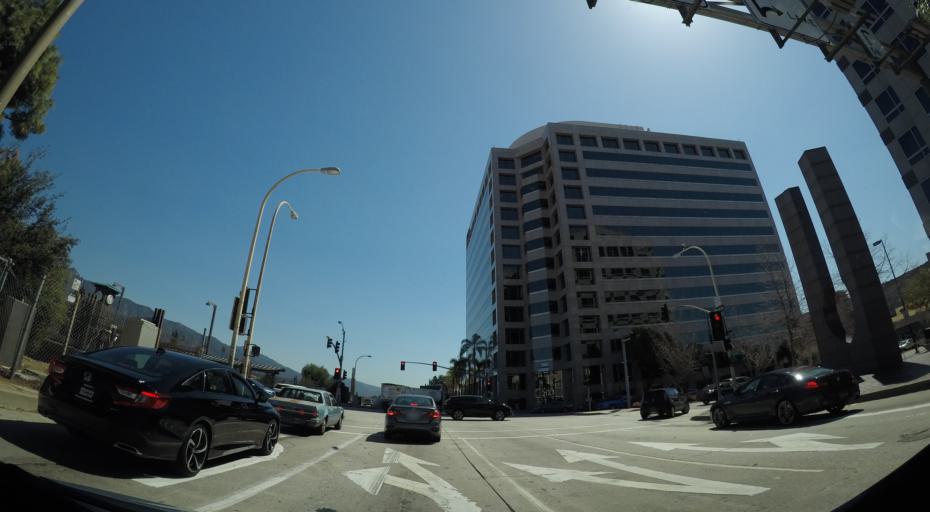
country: US
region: California
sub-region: Los Angeles County
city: Pasadena
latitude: 34.1513
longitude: -118.1328
